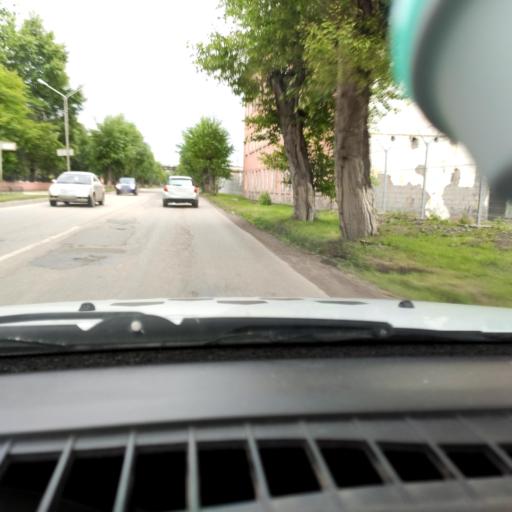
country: RU
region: Perm
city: Chusovoy
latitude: 58.2946
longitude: 57.8139
